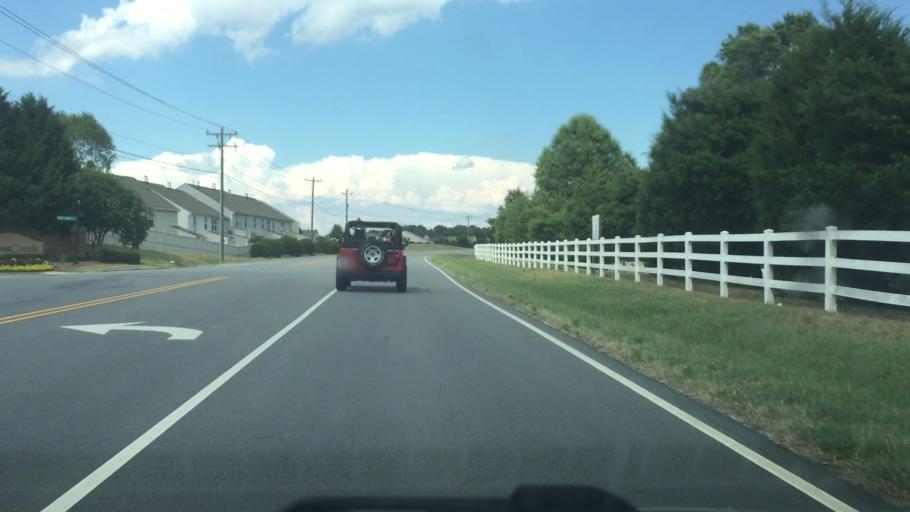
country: US
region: North Carolina
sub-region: Mecklenburg County
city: Huntersville
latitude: 35.4282
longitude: -80.7371
